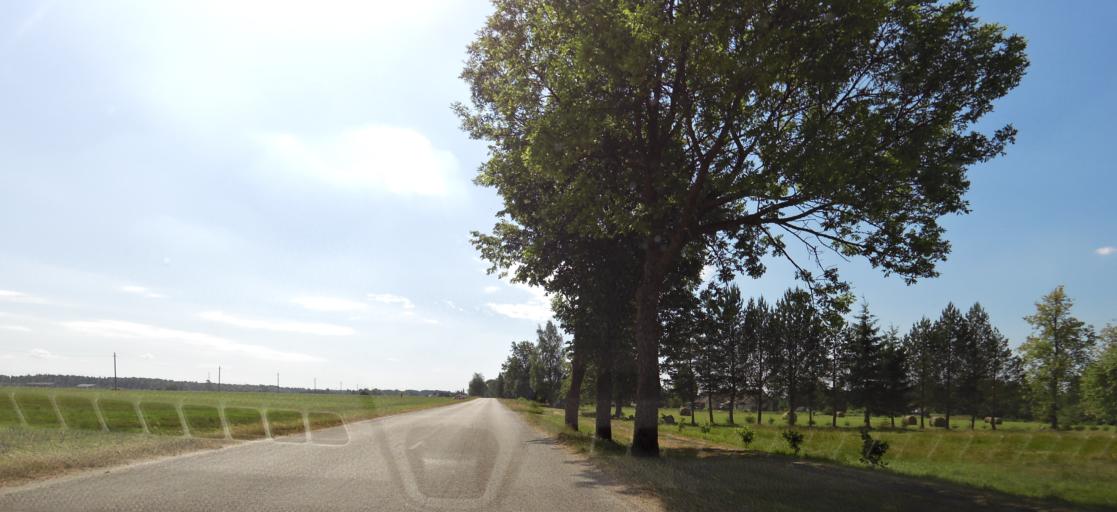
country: LT
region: Panevezys
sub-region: Birzai
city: Birzai
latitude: 56.2008
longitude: 24.9209
